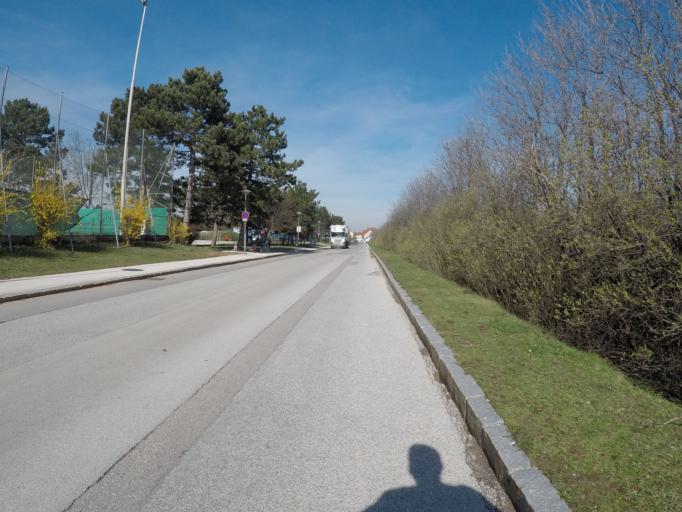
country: AT
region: Lower Austria
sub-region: Politischer Bezirk Modling
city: Vosendorf
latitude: 48.1169
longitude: 16.3375
